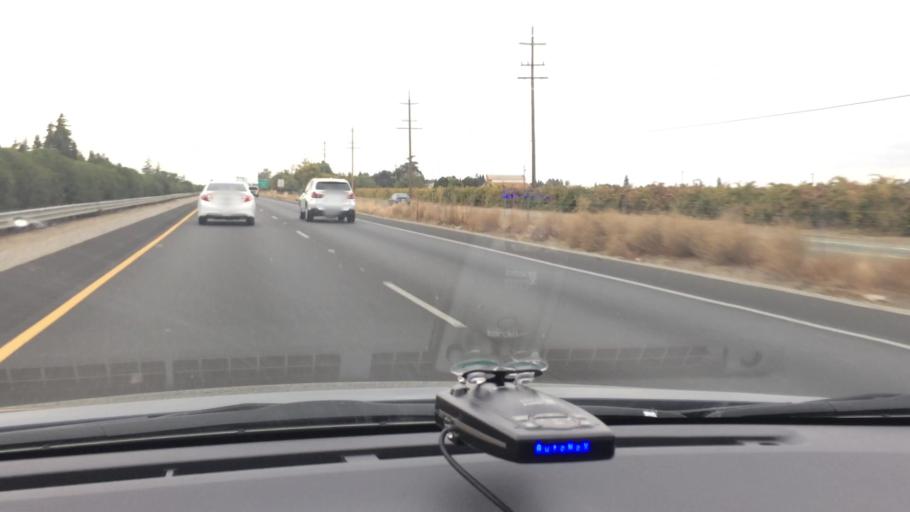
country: US
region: California
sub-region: San Joaquin County
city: Lodi
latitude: 38.1650
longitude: -121.2619
